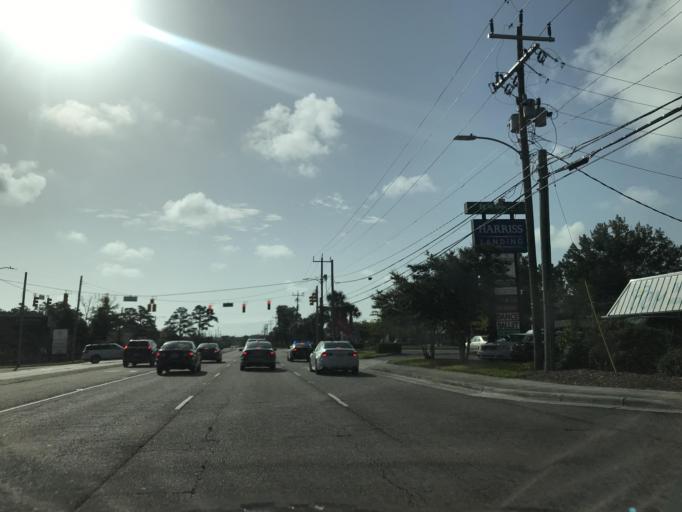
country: US
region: North Carolina
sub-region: New Hanover County
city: Wilmington
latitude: 34.2140
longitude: -77.9001
